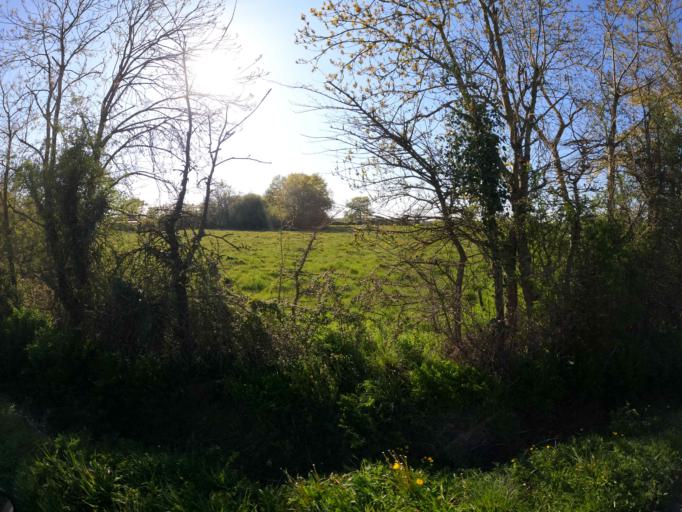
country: FR
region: Pays de la Loire
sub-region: Departement de la Vendee
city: Beaurepaire
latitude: 46.9239
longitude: -1.1164
